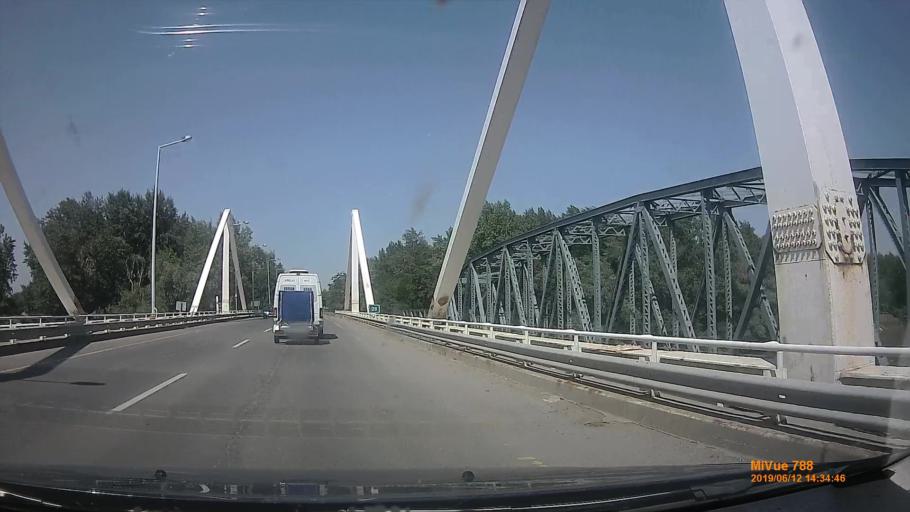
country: HU
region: Csongrad
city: Kiszombor
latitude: 46.2024
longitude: 20.4532
